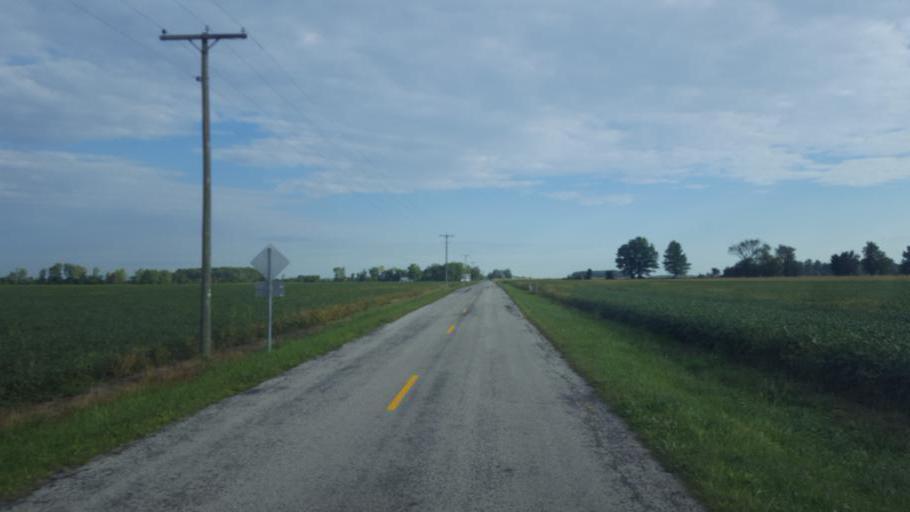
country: US
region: Ohio
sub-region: Crawford County
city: Galion
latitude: 40.6911
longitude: -82.9097
